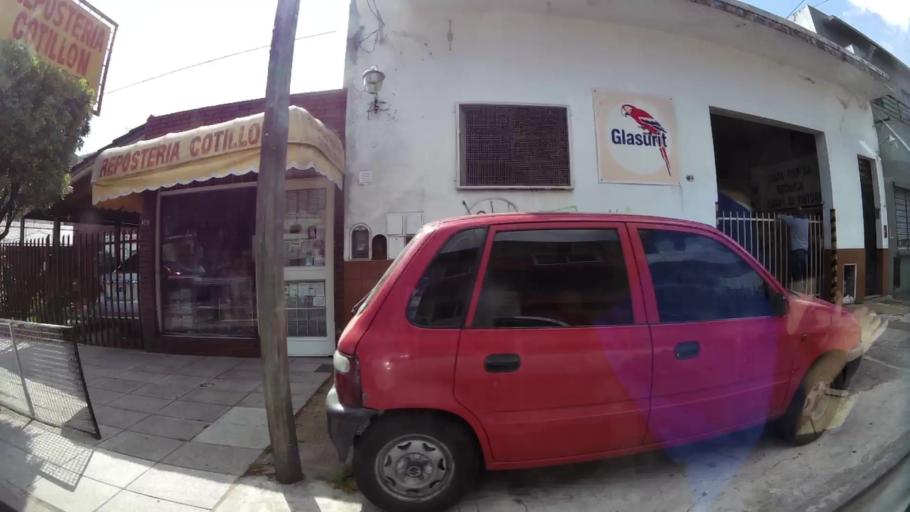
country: AR
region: Buenos Aires
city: San Justo
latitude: -34.6502
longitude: -58.5494
